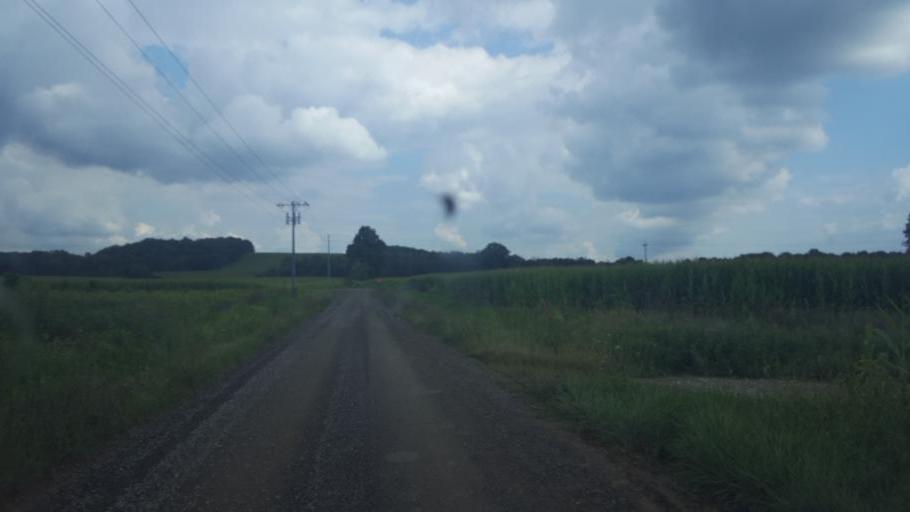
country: US
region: Ohio
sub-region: Knox County
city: Oak Hill
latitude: 40.4219
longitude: -82.2463
